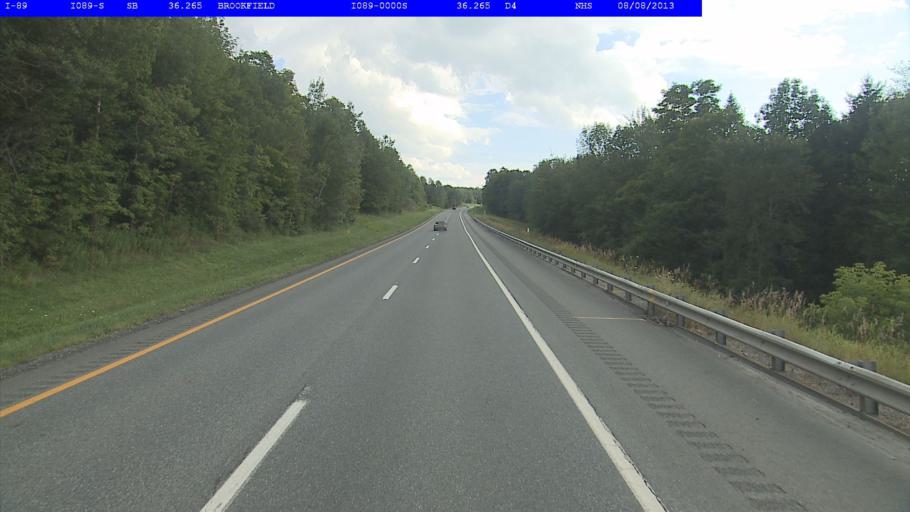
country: US
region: Vermont
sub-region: Orange County
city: Randolph
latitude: 44.0220
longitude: -72.6179
